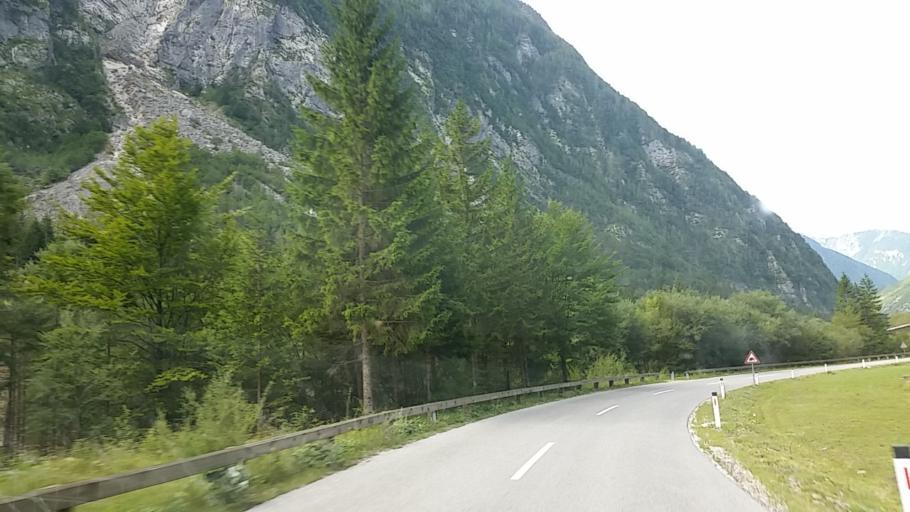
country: SI
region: Kranjska Gora
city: Kranjska Gora
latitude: 46.3661
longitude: 13.7208
